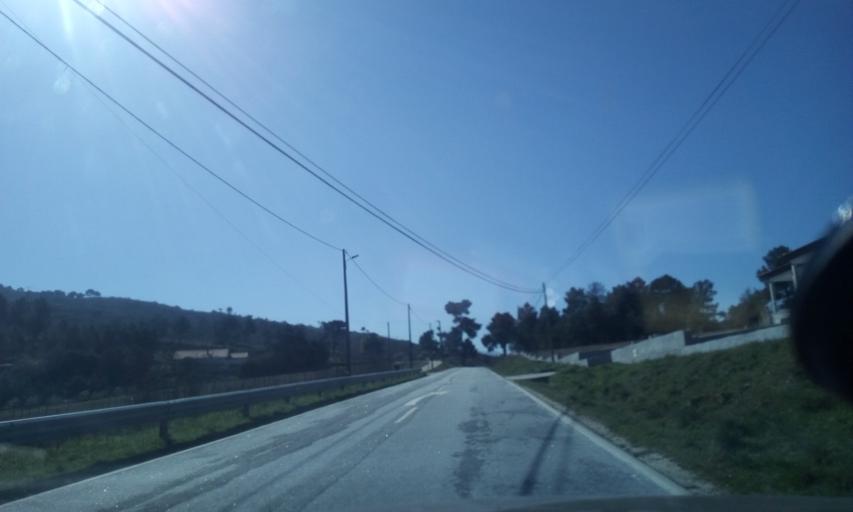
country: PT
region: Guarda
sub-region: Celorico da Beira
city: Celorico da Beira
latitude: 40.6091
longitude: -7.4169
